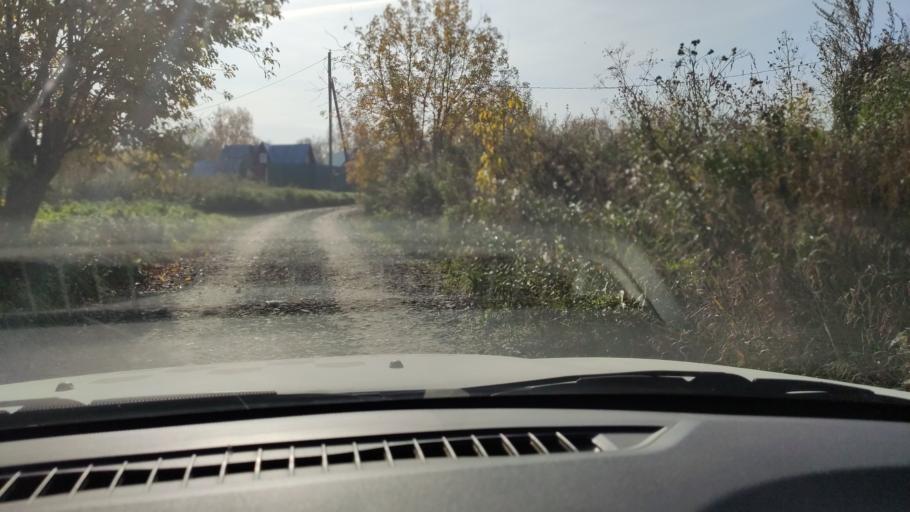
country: RU
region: Perm
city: Sylva
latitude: 58.0468
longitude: 56.7379
